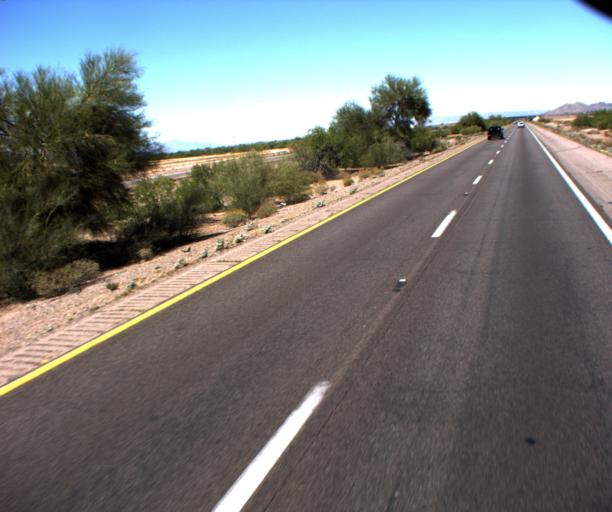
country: US
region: Arizona
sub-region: Pinal County
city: Casa Blanca
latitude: 33.0876
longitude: -111.8184
